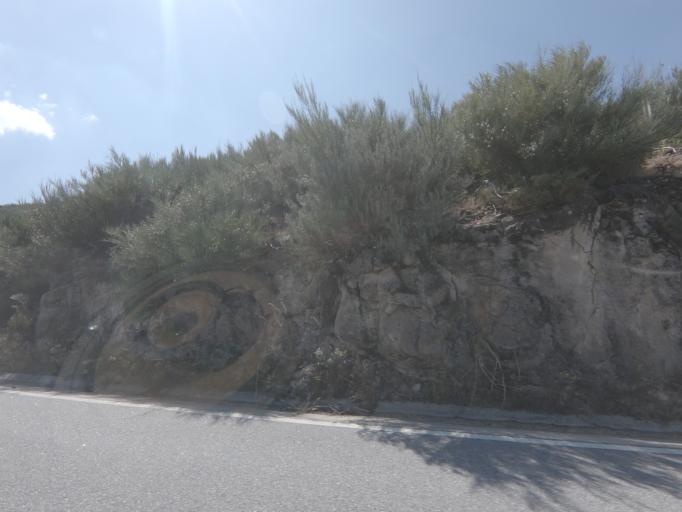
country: PT
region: Viseu
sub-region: Tarouca
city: Tarouca
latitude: 40.9923
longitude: -7.7798
